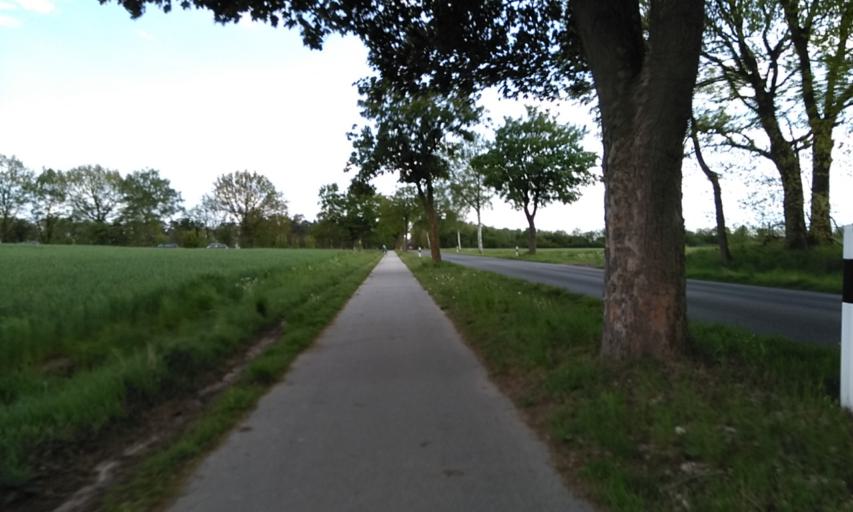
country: DE
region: Lower Saxony
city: Buxtehude
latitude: 53.4440
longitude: 9.6658
